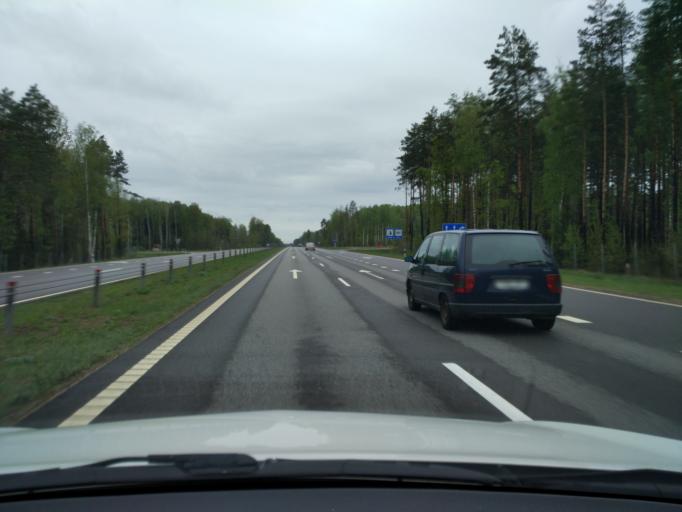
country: BY
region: Mogilev
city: Asipovichy
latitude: 53.3854
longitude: 28.5514
